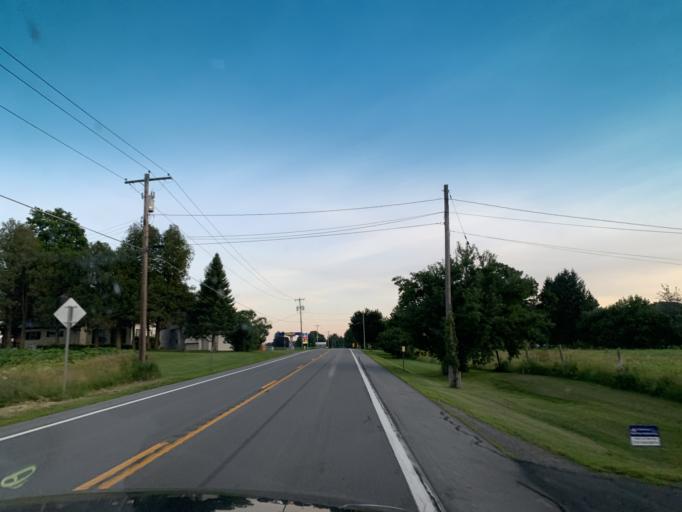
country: US
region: New York
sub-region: Oneida County
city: Chadwicks
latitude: 42.8964
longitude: -75.2448
